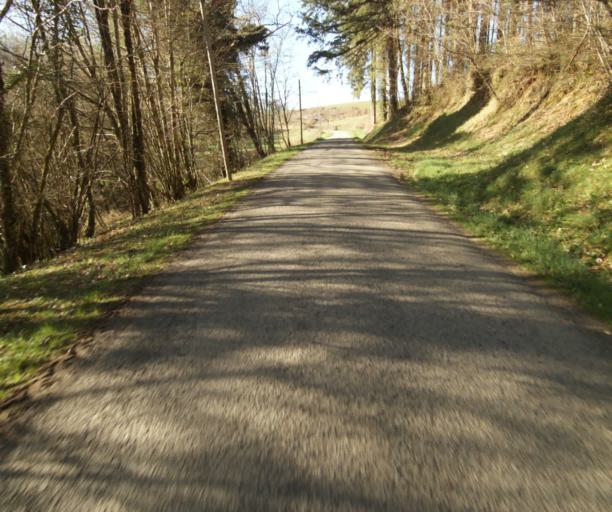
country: FR
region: Limousin
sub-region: Departement de la Correze
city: Seilhac
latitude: 45.3901
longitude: 1.7584
